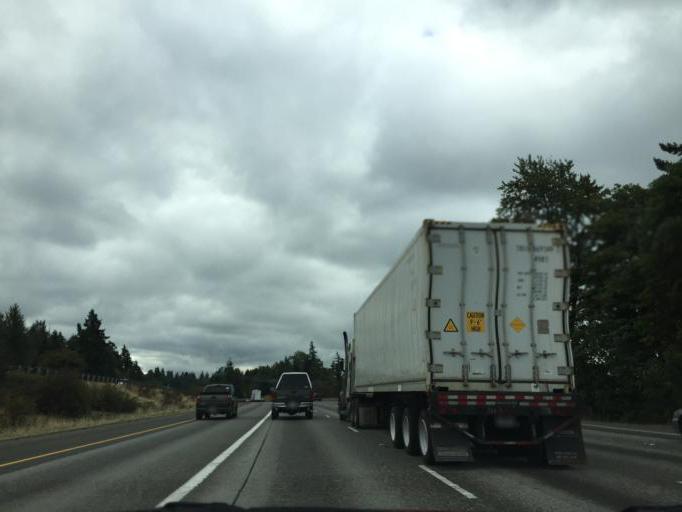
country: US
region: Washington
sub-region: King County
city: Lakeland North
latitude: 47.3593
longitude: -122.2964
